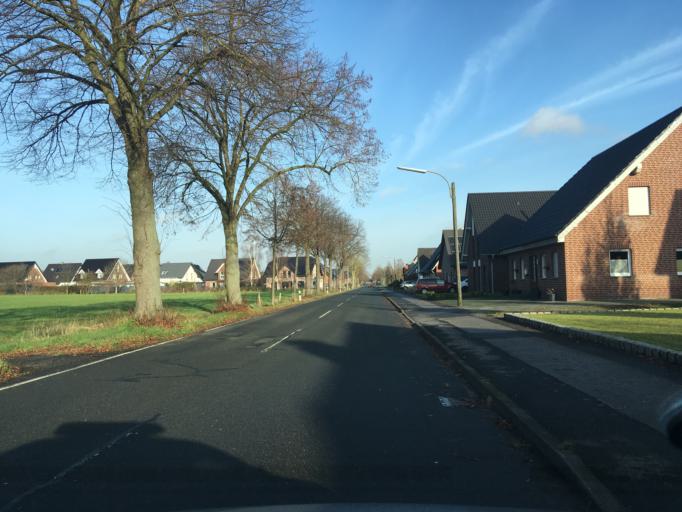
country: DE
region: North Rhine-Westphalia
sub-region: Regierungsbezirk Munster
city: Gescher
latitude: 51.9444
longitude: 6.9868
